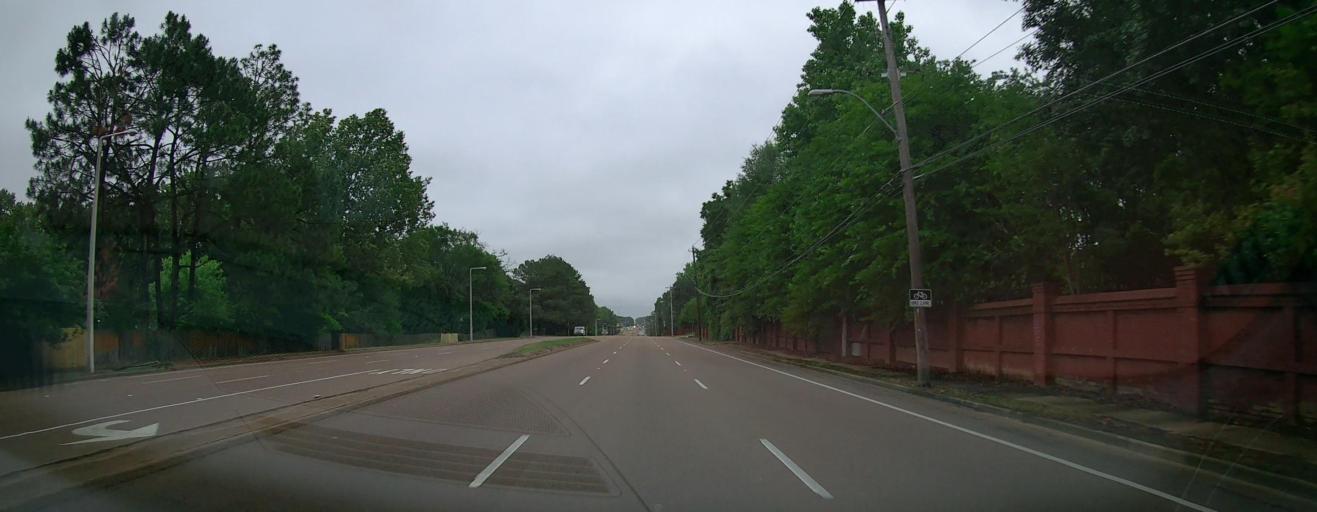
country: US
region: Tennessee
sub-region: Shelby County
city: Germantown
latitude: 35.0309
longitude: -89.8314
